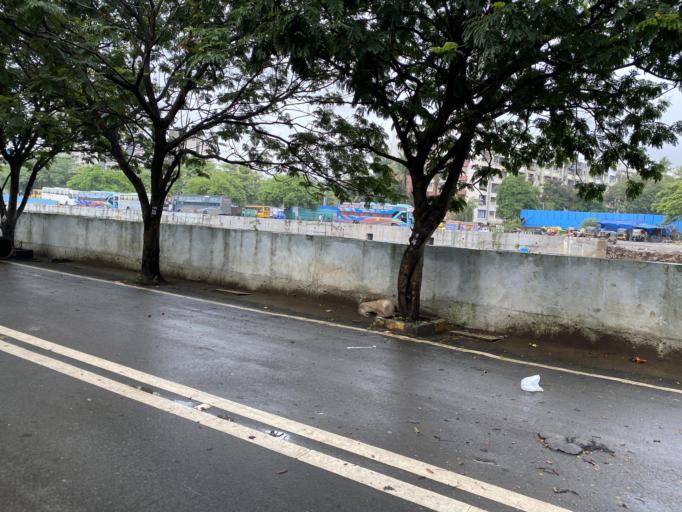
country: IN
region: Maharashtra
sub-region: Mumbai Suburban
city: Borivli
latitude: 19.2610
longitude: 72.8550
